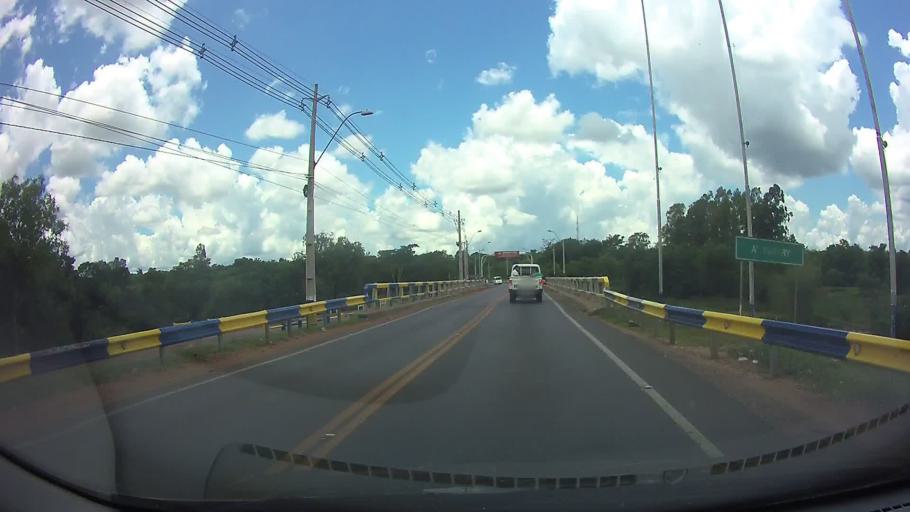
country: PY
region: Central
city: Capiata
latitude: -25.2927
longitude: -57.4463
